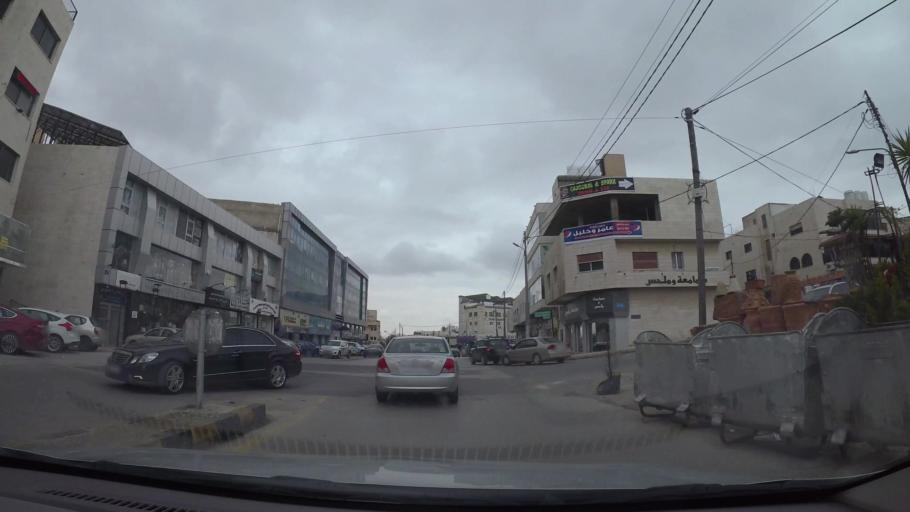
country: JO
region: Amman
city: Wadi as Sir
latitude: 31.9803
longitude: 35.8480
